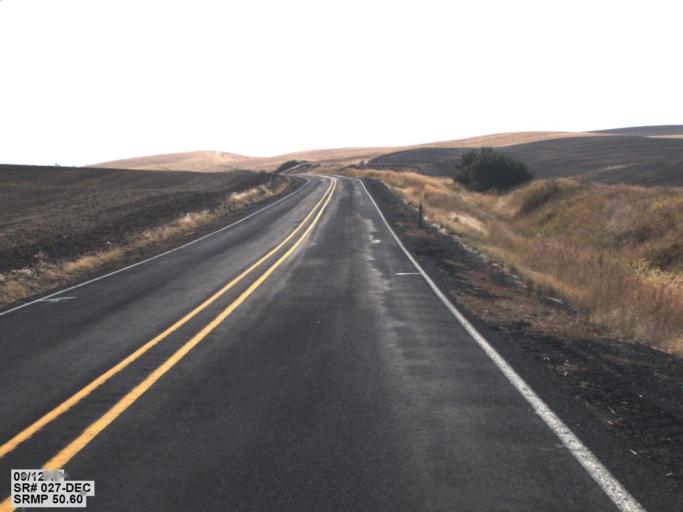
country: US
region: Idaho
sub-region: Benewah County
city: Plummer
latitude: 47.2331
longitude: -117.1134
